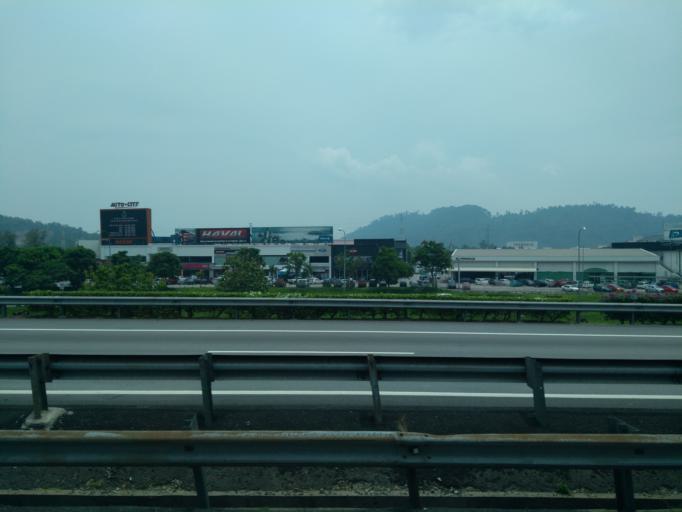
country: MY
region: Penang
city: Juru
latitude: 5.3397
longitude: 100.4314
